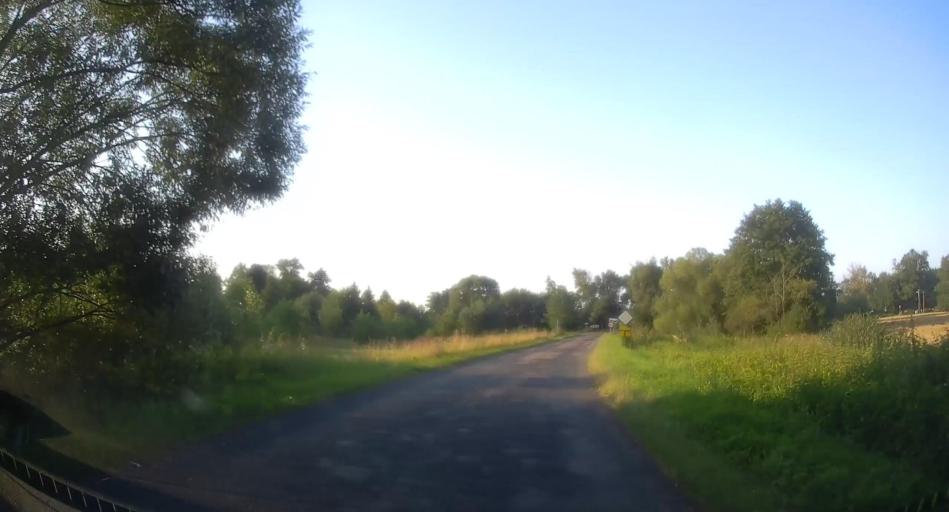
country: PL
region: Lodz Voivodeship
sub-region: Powiat skierniewicki
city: Kaweczyn Nowy
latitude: 51.8992
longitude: 20.2984
